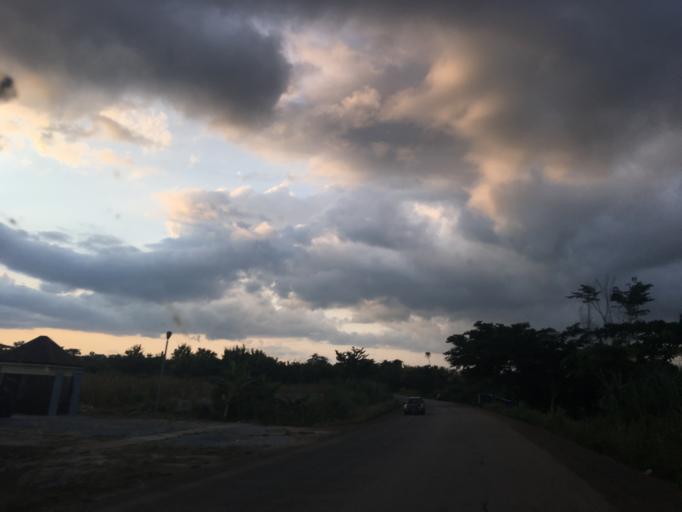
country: GH
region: Western
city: Bibiani
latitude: 6.7600
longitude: -2.5041
